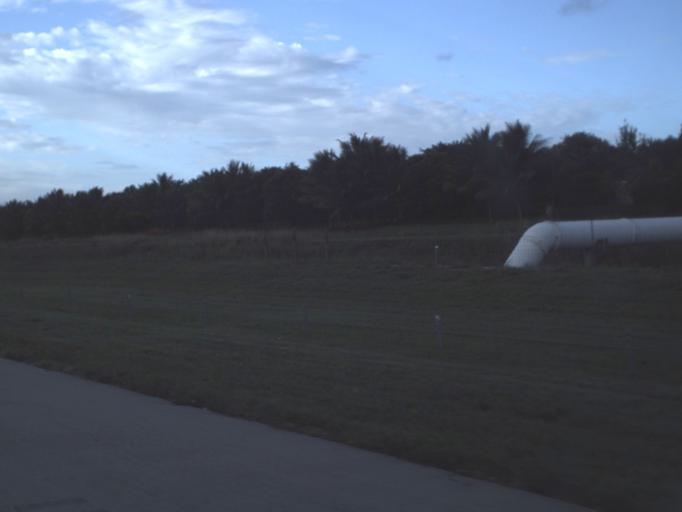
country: US
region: Florida
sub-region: Palm Beach County
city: Kings Point
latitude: 26.4281
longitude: -80.1722
